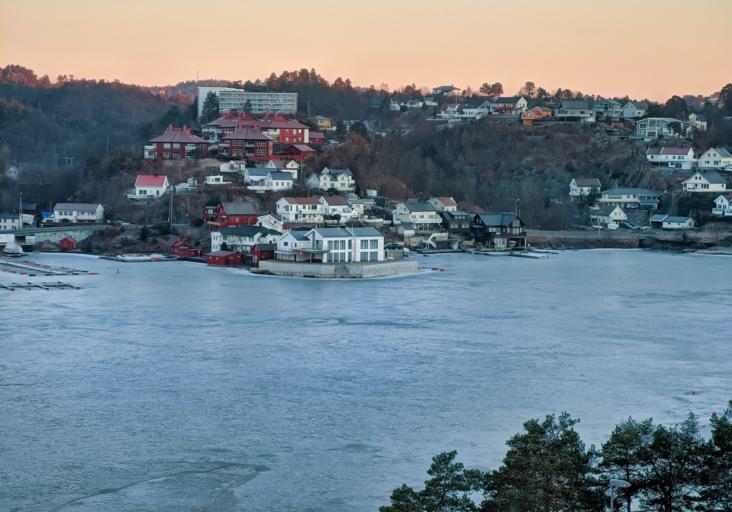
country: NO
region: Aust-Agder
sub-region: Arendal
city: Arendal
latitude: 58.4406
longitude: 8.7409
